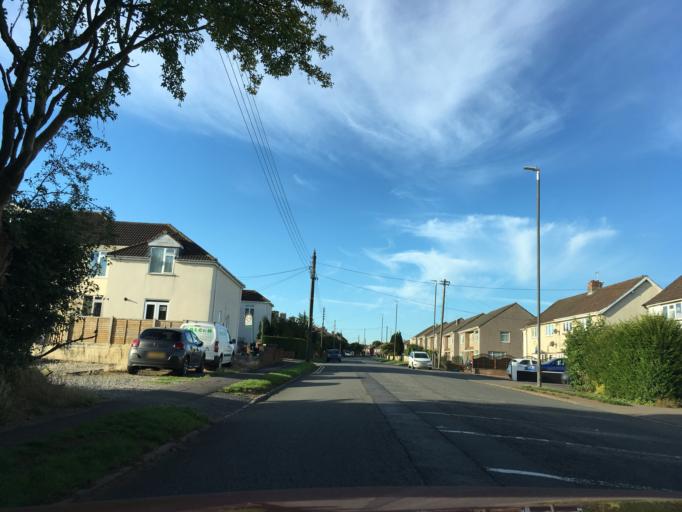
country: GB
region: England
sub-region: South Gloucestershire
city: Mangotsfield
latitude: 51.4920
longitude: -2.4856
